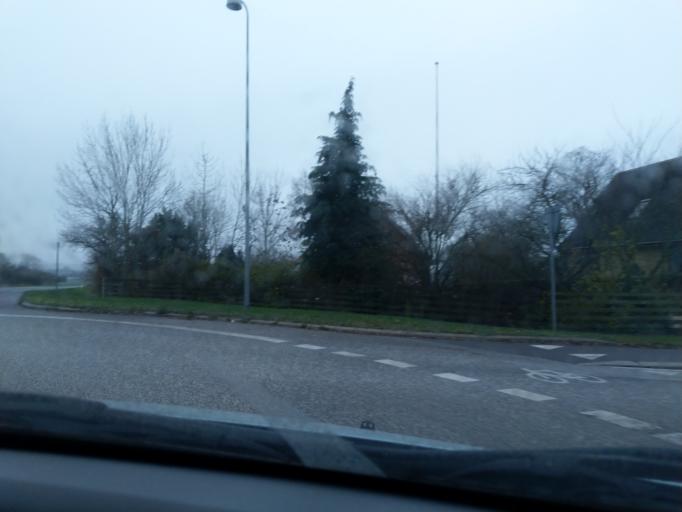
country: DK
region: Zealand
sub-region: Vordingborg Kommune
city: Orslev
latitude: 55.1210
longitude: 11.9692
